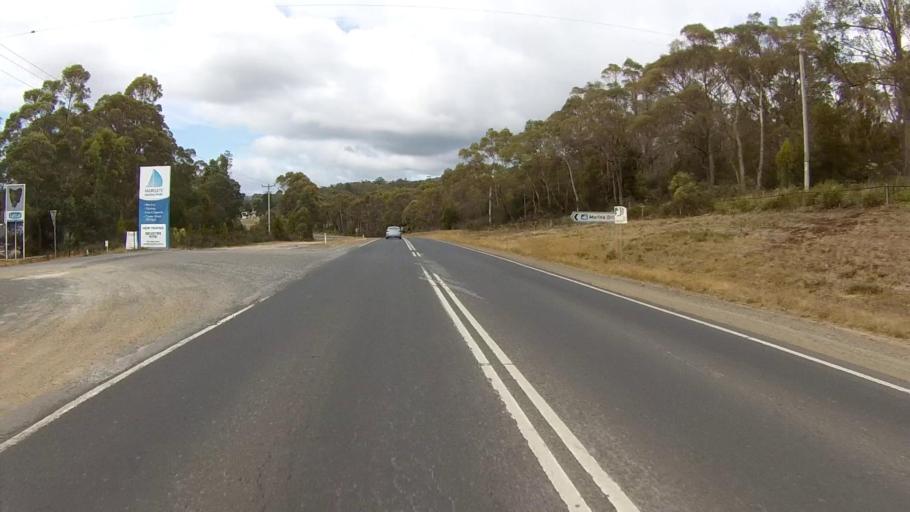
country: AU
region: Tasmania
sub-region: Kingborough
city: Margate
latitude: -43.0479
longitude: 147.2635
